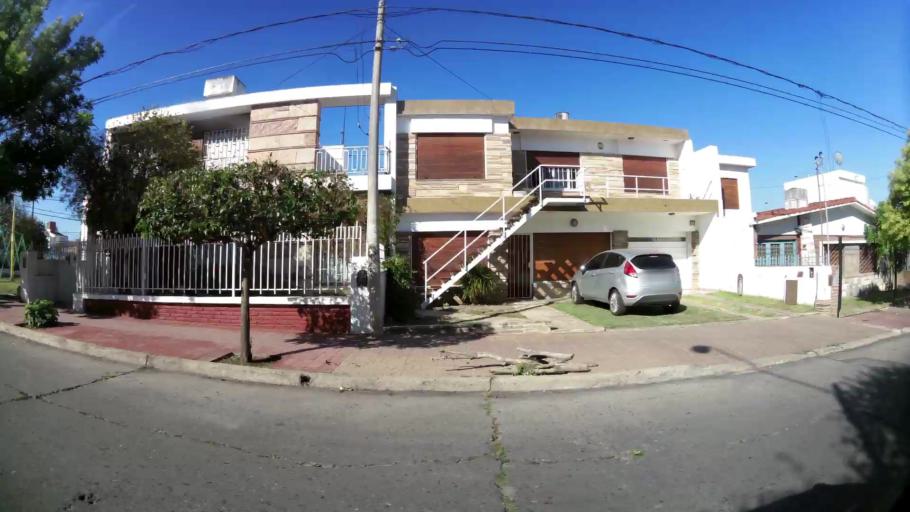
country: AR
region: Cordoba
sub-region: Departamento de Capital
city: Cordoba
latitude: -31.4245
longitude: -64.1391
